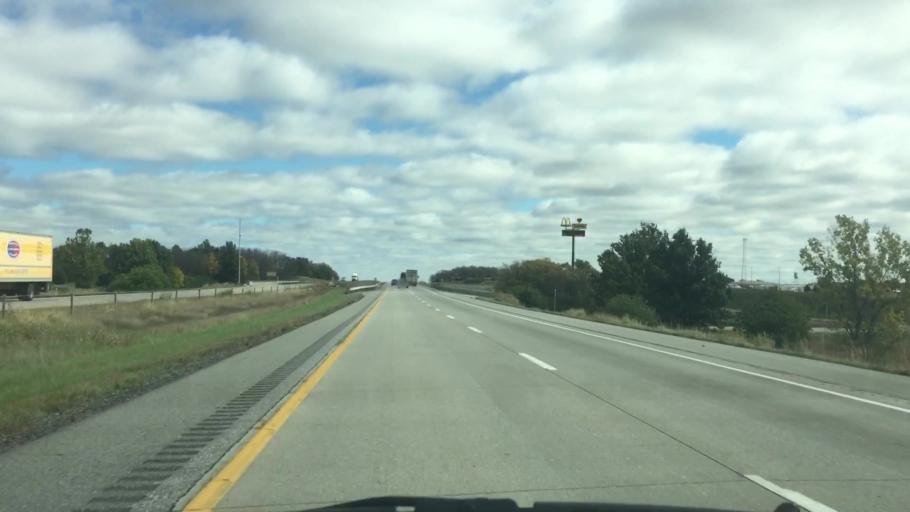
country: US
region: Iowa
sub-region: Jasper County
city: Newton
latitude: 41.6826
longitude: -93.0021
